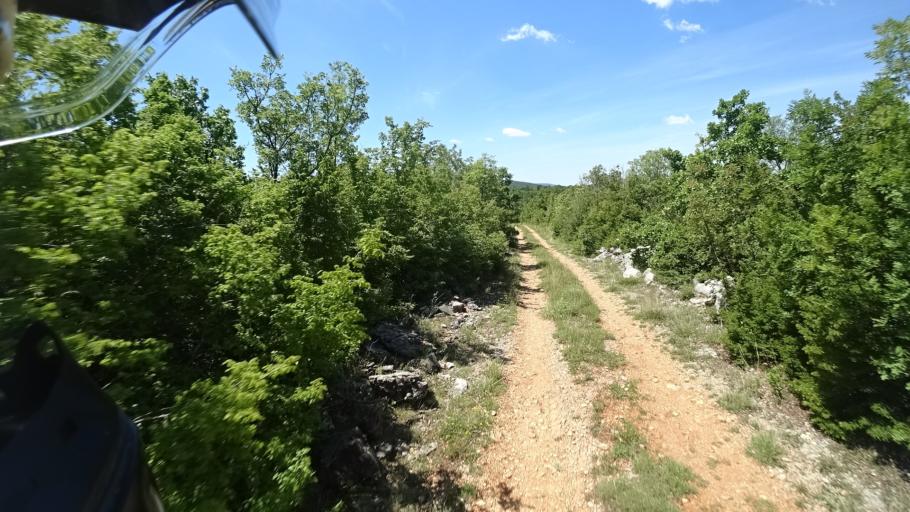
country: HR
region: Sibensko-Kniniska
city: Knin
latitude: 44.0059
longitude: 16.3061
